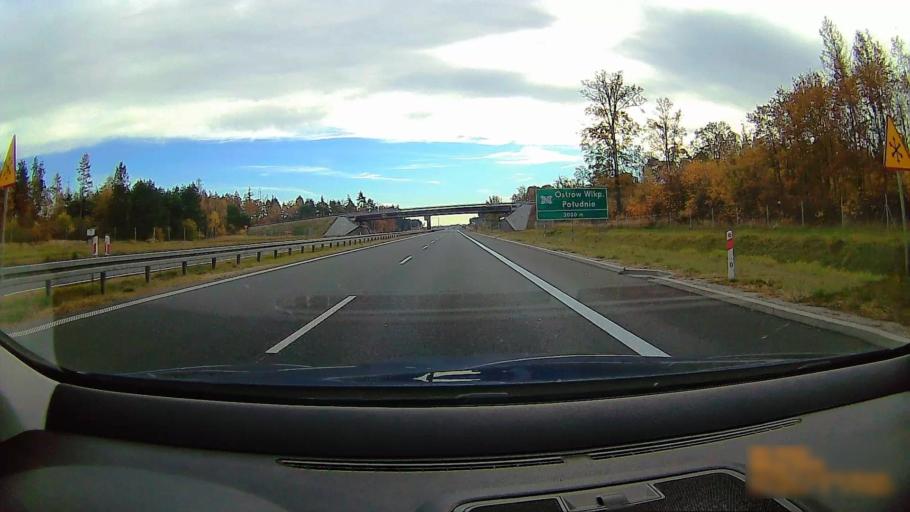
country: PL
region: Greater Poland Voivodeship
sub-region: Powiat ostrowski
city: Ostrow Wielkopolski
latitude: 51.6565
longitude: 17.8645
